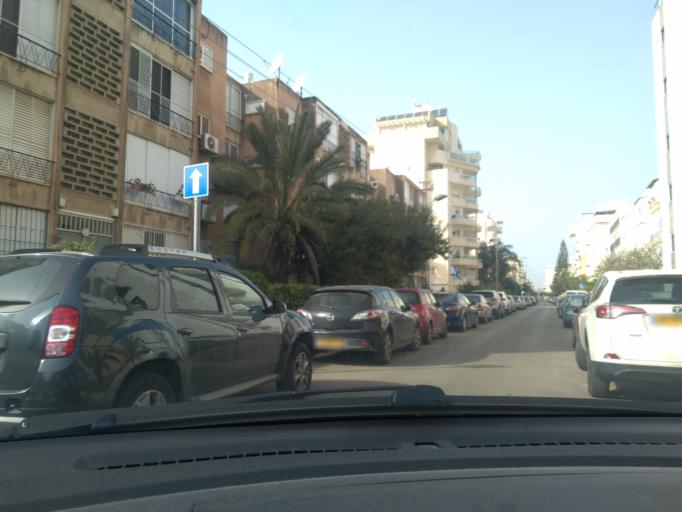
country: IL
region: Central District
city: Netanya
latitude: 32.3318
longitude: 34.8576
